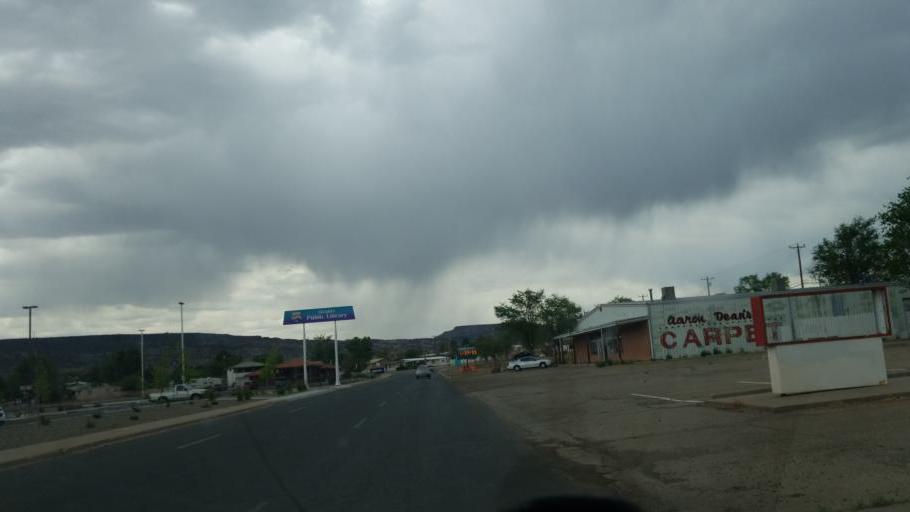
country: US
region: New Mexico
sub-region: Cibola County
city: Grants
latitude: 35.1595
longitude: -107.8424
